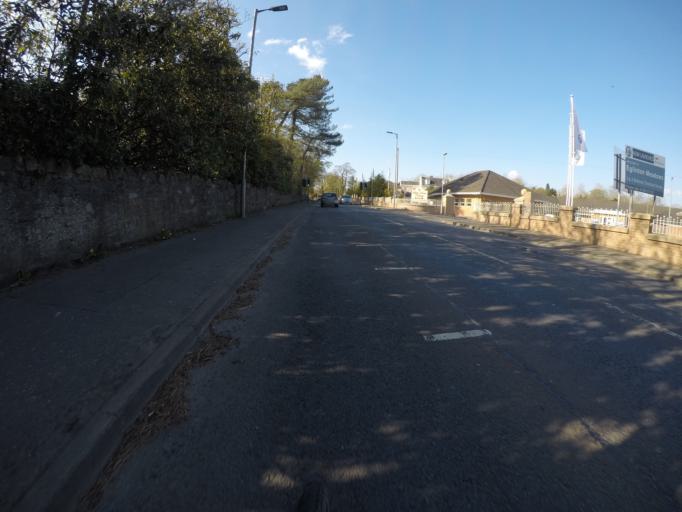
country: GB
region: Scotland
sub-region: North Ayrshire
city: Kilwinning
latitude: 55.6501
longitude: -4.6888
